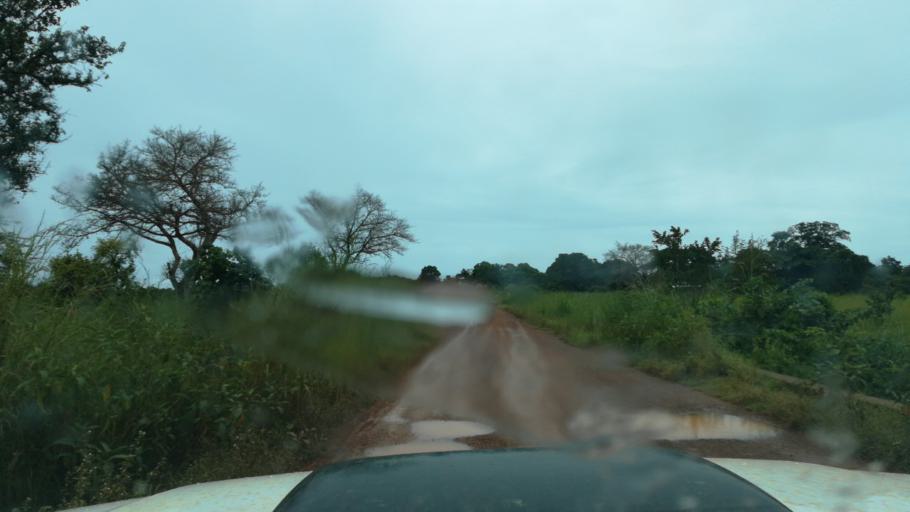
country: ZM
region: Luapula
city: Mwense
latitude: -10.1781
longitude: 28.1232
